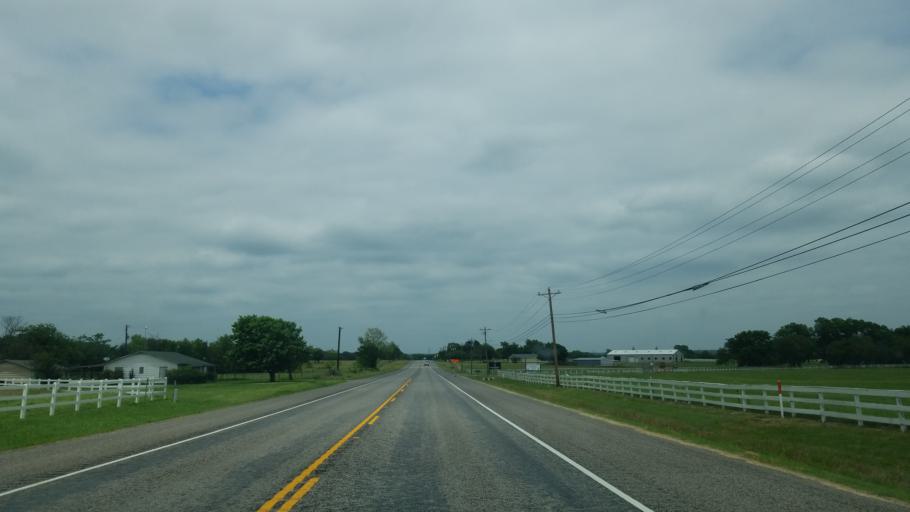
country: US
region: Texas
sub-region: Denton County
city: Krugerville
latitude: 33.3018
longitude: -97.0685
